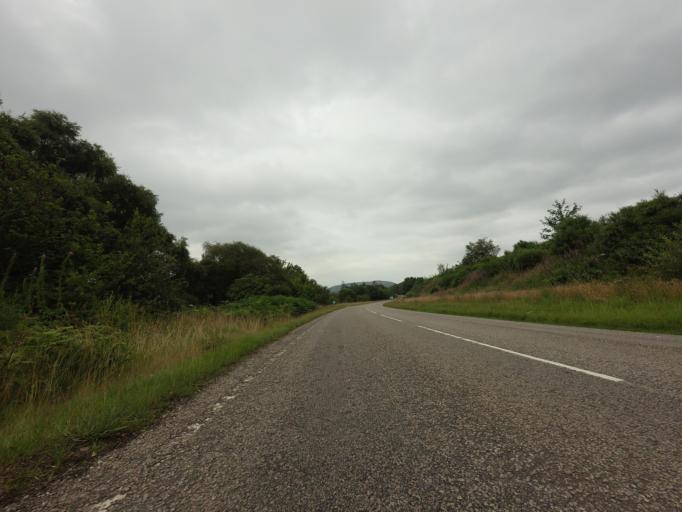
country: GB
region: Scotland
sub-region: Highland
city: Alness
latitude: 57.9098
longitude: -4.3704
